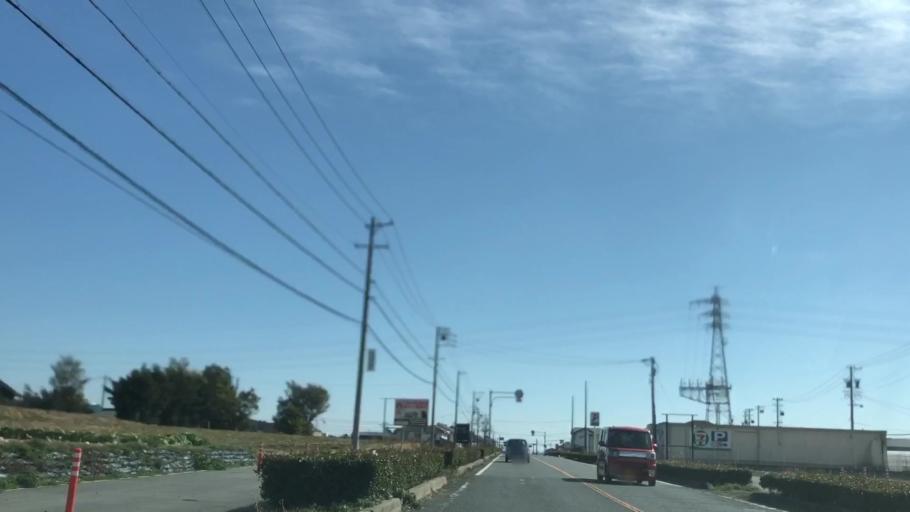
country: JP
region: Aichi
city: Toyohashi
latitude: 34.7094
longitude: 137.4095
